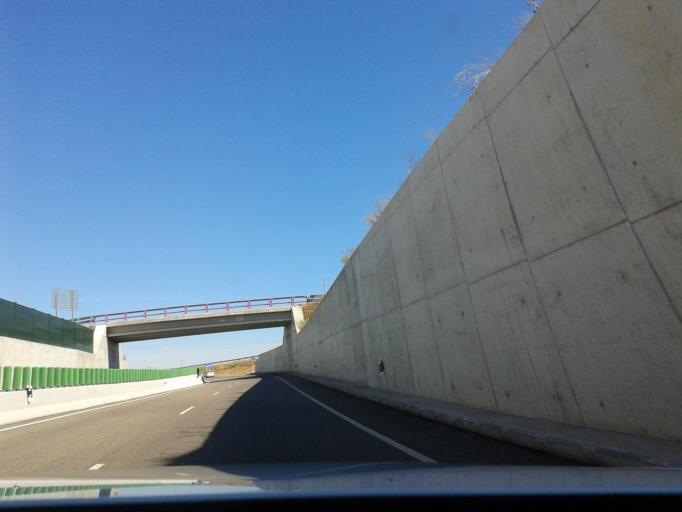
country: ES
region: Castille-La Mancha
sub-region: Provincia de Guadalajara
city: Azuqueca de Henares
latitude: 40.5790
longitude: -3.2595
